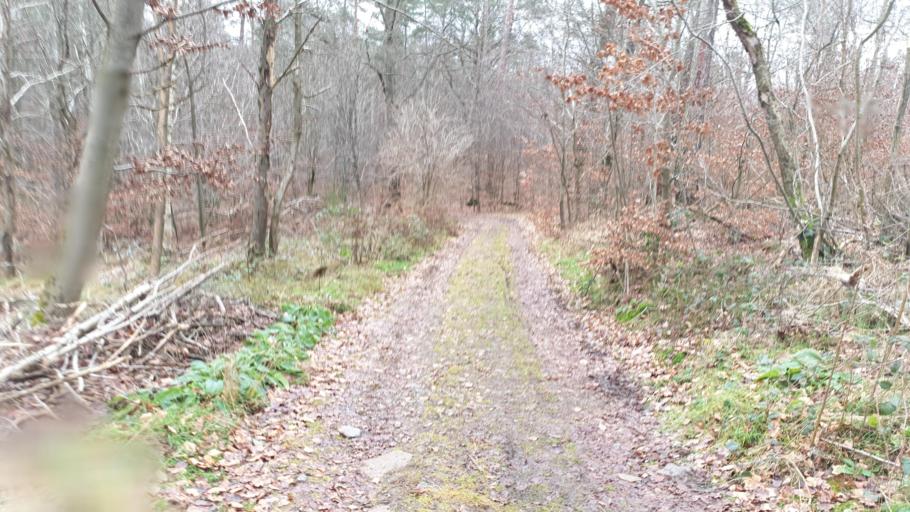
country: DE
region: Saxony
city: Hohburg
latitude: 51.4223
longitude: 12.7945
